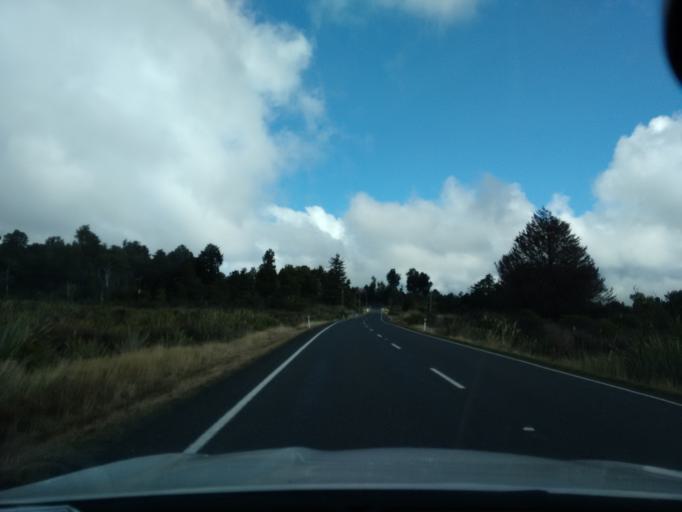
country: NZ
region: Manawatu-Wanganui
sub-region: Ruapehu District
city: Waiouru
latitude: -39.2322
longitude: 175.3936
